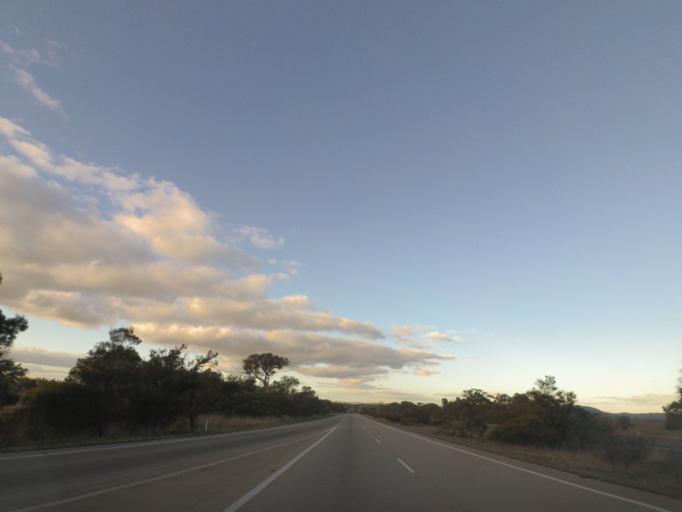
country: AU
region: New South Wales
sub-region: Yass Valley
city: Yass
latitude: -34.7741
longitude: 148.7368
